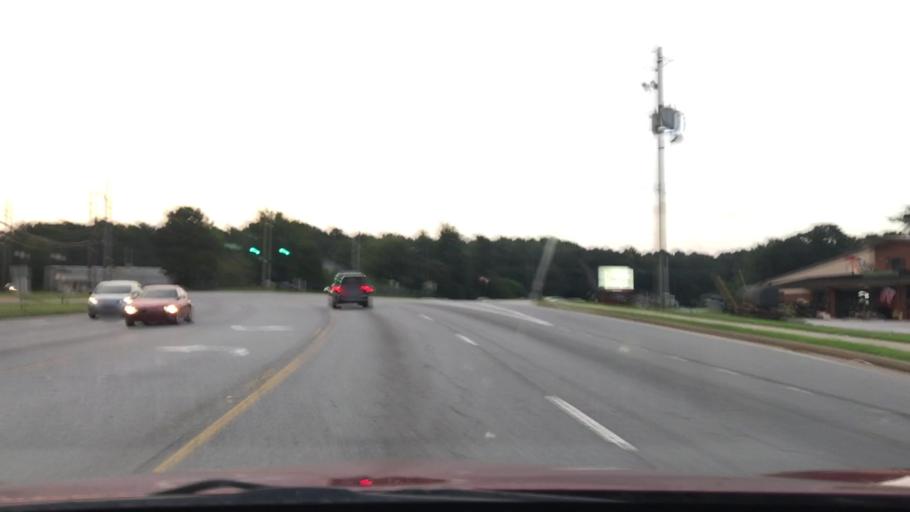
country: US
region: Georgia
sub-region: Gwinnett County
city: Lawrenceville
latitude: 33.9887
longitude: -83.9842
